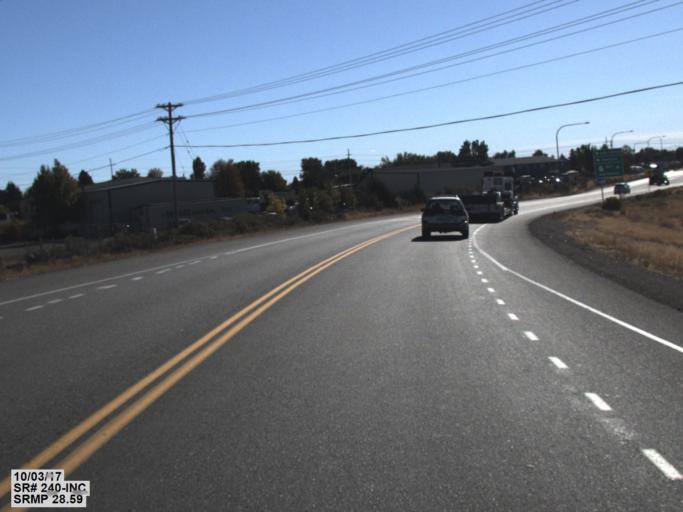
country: US
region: Washington
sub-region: Benton County
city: Richland
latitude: 46.3117
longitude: -119.2888
